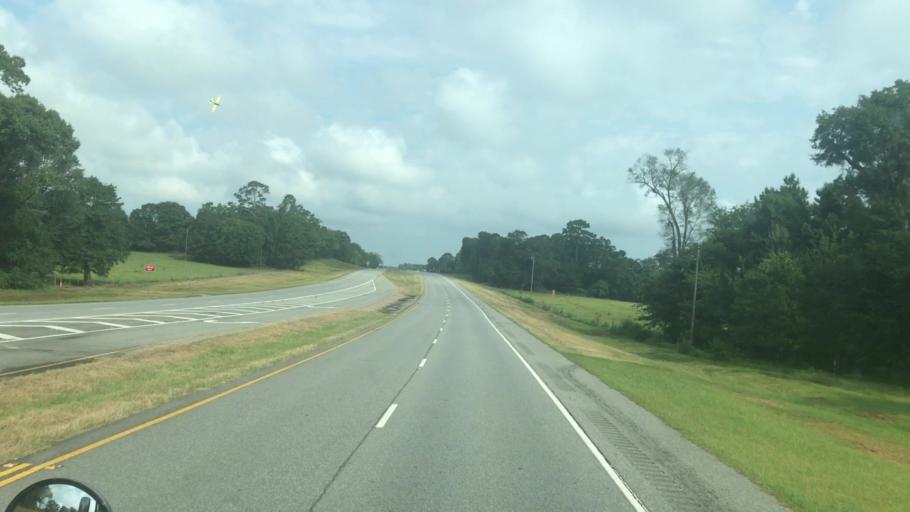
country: US
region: Georgia
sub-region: Miller County
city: Colquitt
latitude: 31.2467
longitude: -84.7933
